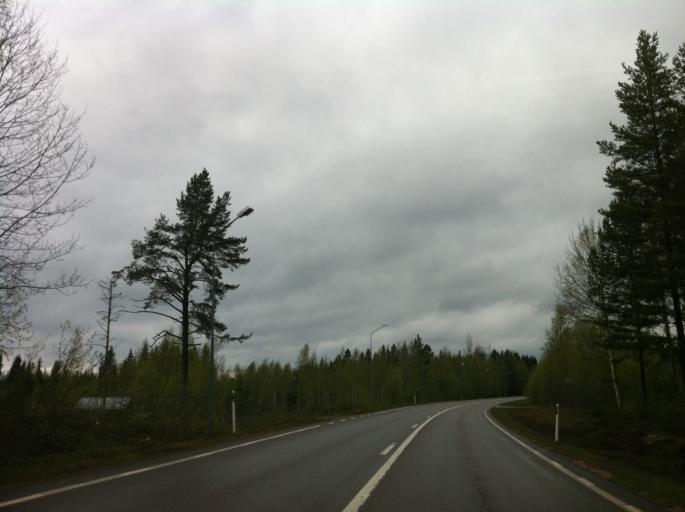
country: SE
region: Jaemtland
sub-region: Harjedalens Kommun
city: Sveg
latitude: 62.0625
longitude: 14.2804
